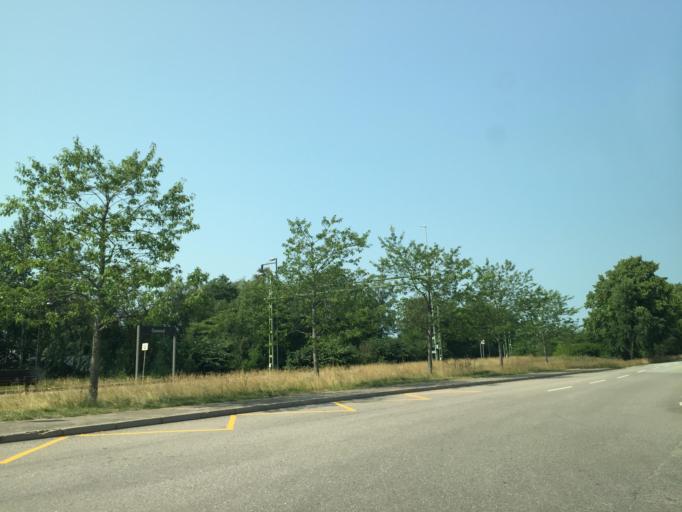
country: SE
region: Vaestra Goetaland
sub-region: Vanersborgs Kommun
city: Vanersborg
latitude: 58.3594
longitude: 12.2745
